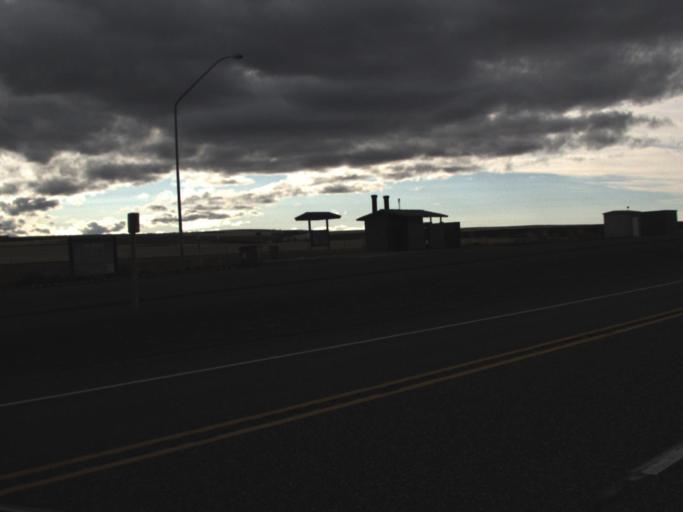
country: US
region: Washington
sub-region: Garfield County
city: Pomeroy
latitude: 46.4359
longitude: -117.4242
